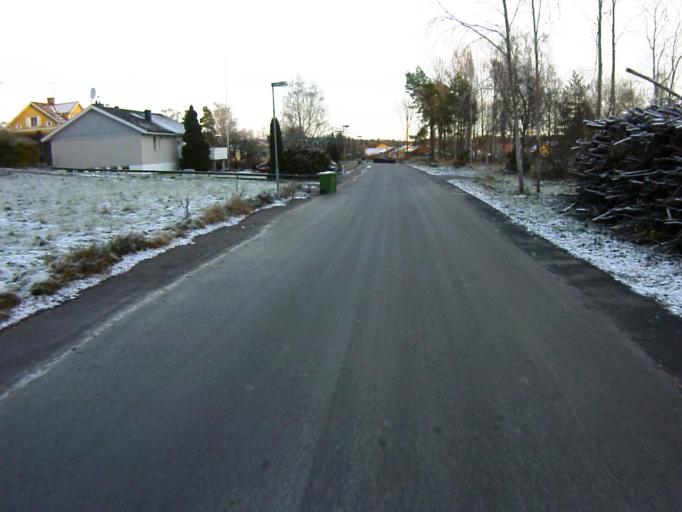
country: SE
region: Soedermanland
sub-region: Eskilstuna Kommun
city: Arla
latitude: 59.3205
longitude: 16.5954
